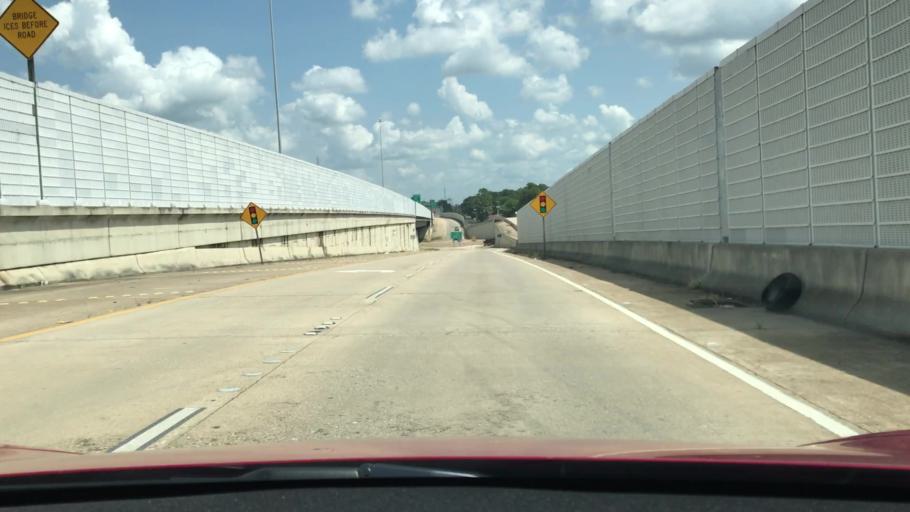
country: US
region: Louisiana
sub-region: Bossier Parish
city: Bossier City
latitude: 32.4795
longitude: -93.7547
